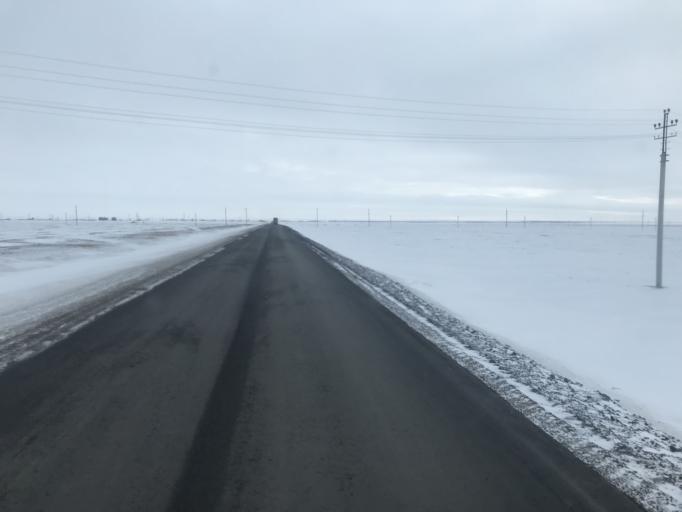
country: RU
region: Orenburg
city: Dombarovskiy
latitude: 49.9528
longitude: 60.0907
